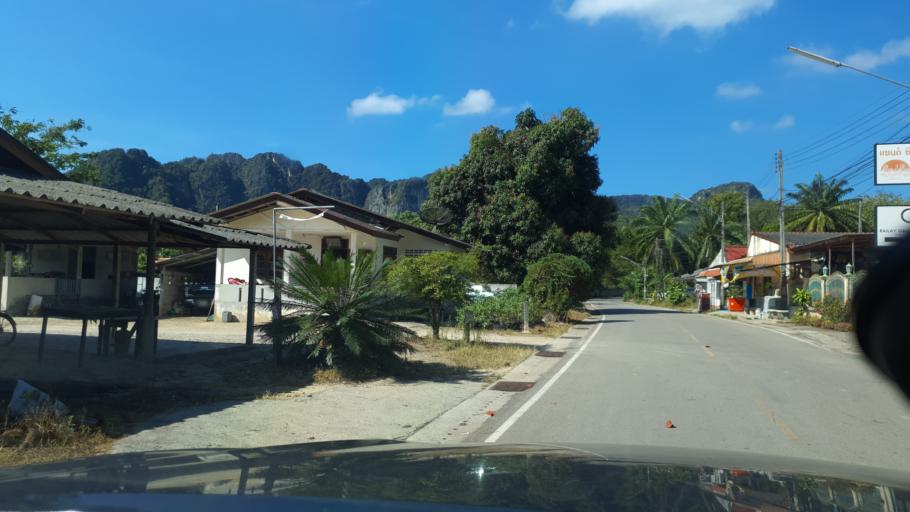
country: TH
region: Phangnga
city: Ban Ao Nang
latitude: 8.0299
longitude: 98.8613
